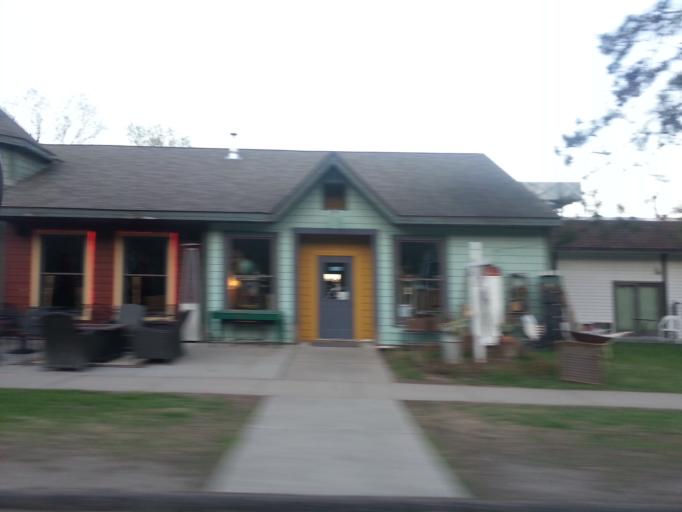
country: US
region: Minnesota
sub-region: Washington County
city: Afton
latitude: 44.9011
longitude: -92.7831
